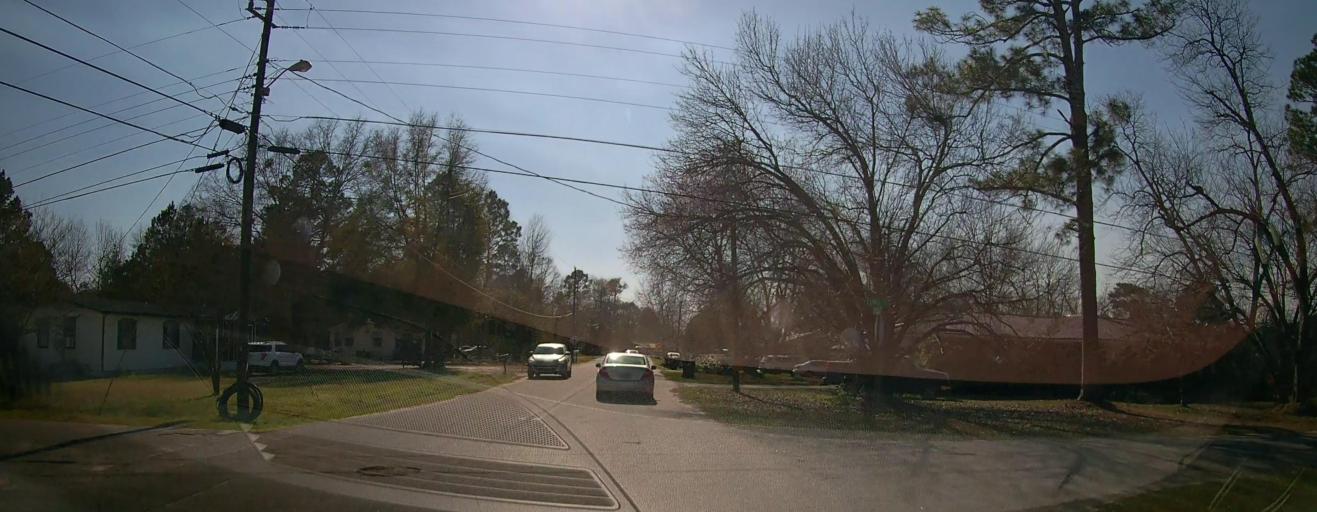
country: US
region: Georgia
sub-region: Macon County
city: Montezuma
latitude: 32.2871
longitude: -84.0138
